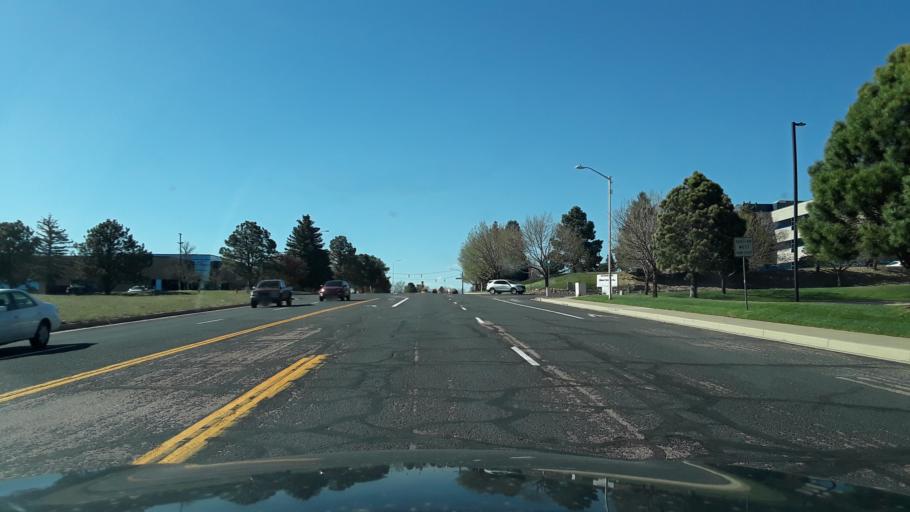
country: US
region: Colorado
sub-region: El Paso County
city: Air Force Academy
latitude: 38.9574
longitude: -104.7905
